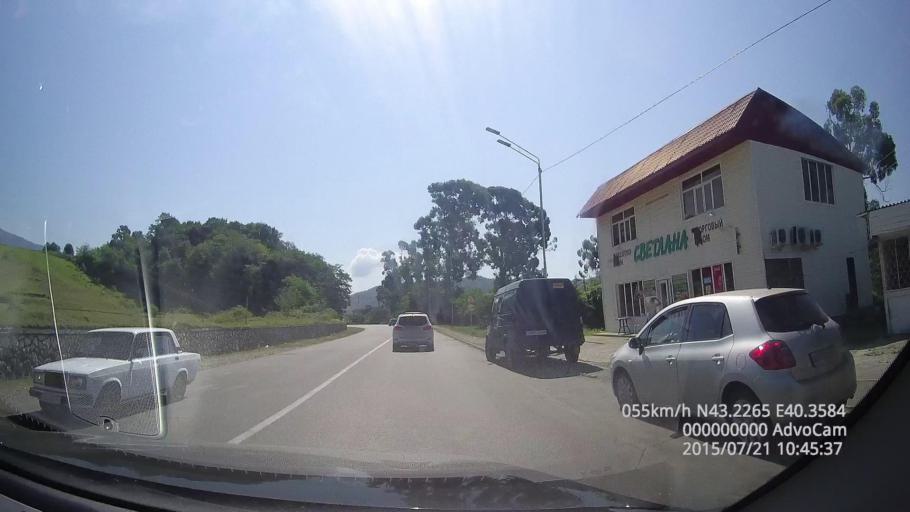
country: GE
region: Abkhazia
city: Bich'vinta
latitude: 43.2264
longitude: 40.3588
